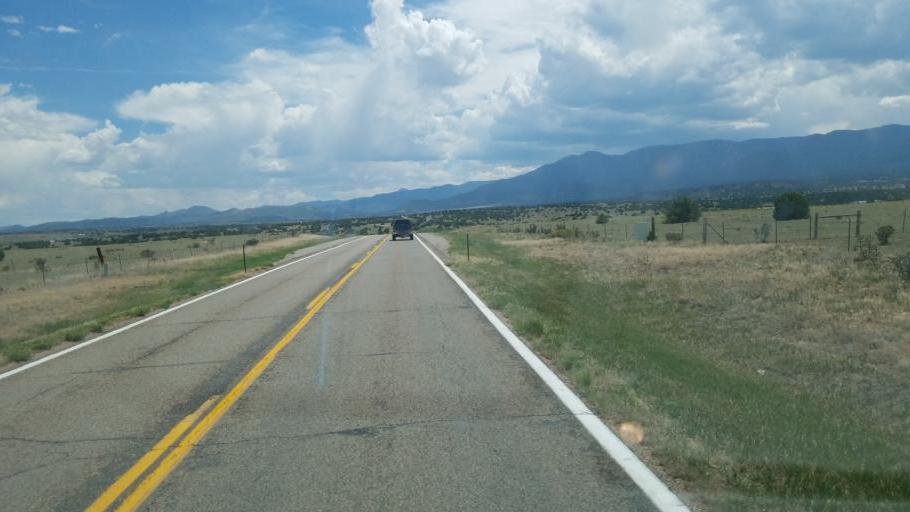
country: US
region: Colorado
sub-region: Fremont County
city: Florence
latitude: 38.3198
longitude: -105.1053
